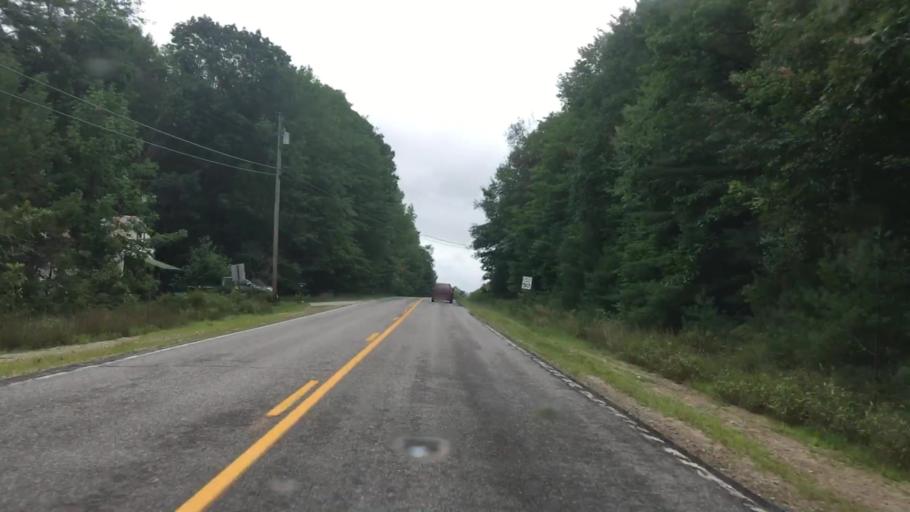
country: US
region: Maine
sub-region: Oxford County
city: Brownfield
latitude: 43.9562
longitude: -70.8975
